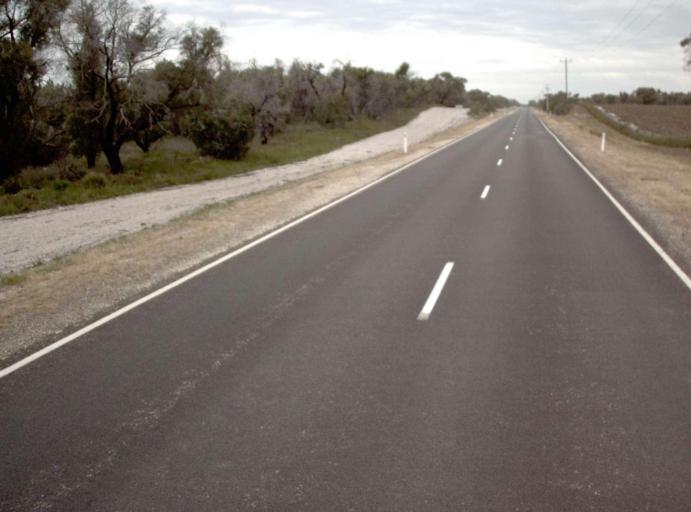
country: AU
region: Victoria
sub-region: Wellington
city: Sale
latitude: -38.1646
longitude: 147.3888
